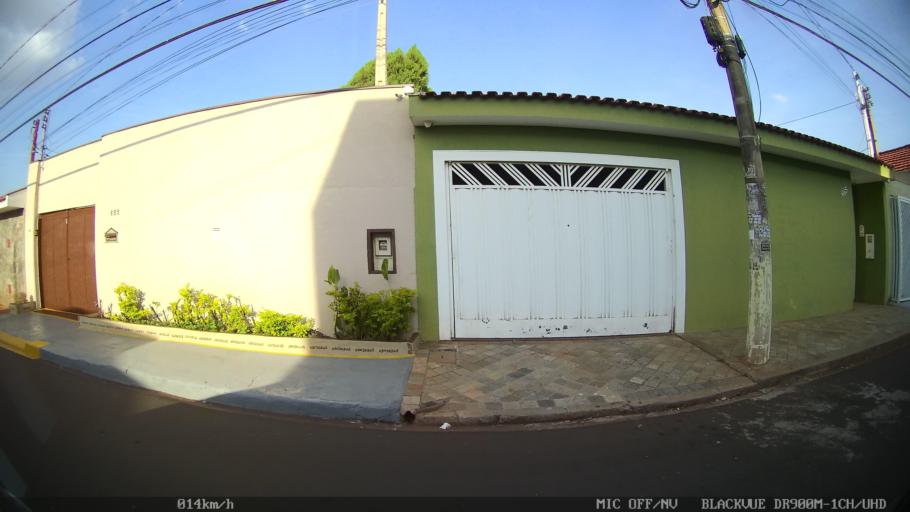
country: BR
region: Sao Paulo
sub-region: Ribeirao Preto
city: Ribeirao Preto
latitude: -21.1716
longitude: -47.8339
